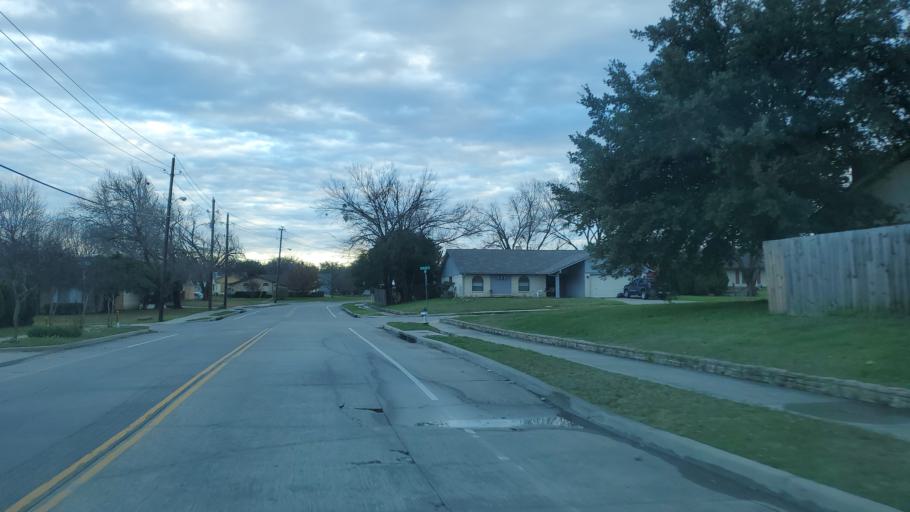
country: US
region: Texas
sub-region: Dallas County
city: Carrollton
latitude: 32.9923
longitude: -96.8829
